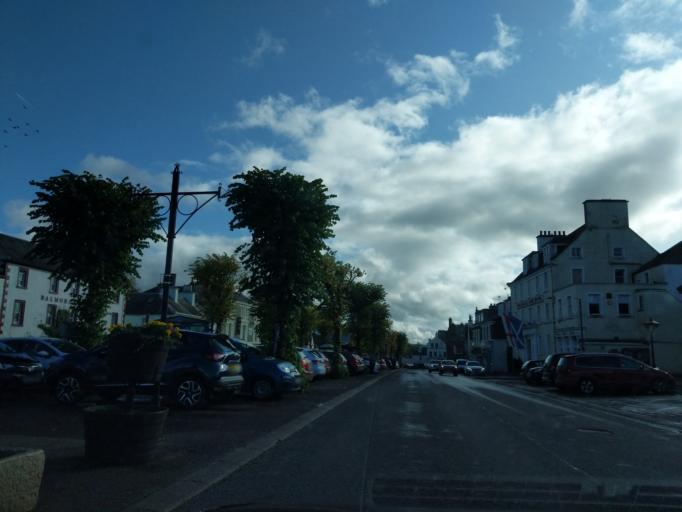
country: GB
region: Scotland
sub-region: Dumfries and Galloway
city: Moffat
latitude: 55.3337
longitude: -3.4449
